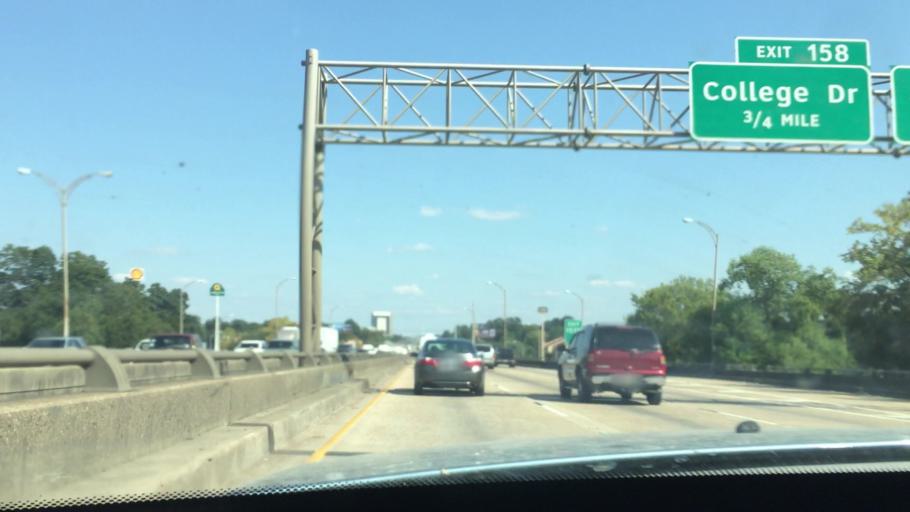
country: US
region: Louisiana
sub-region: East Baton Rouge Parish
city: Baton Rouge
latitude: 30.4245
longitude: -91.1543
